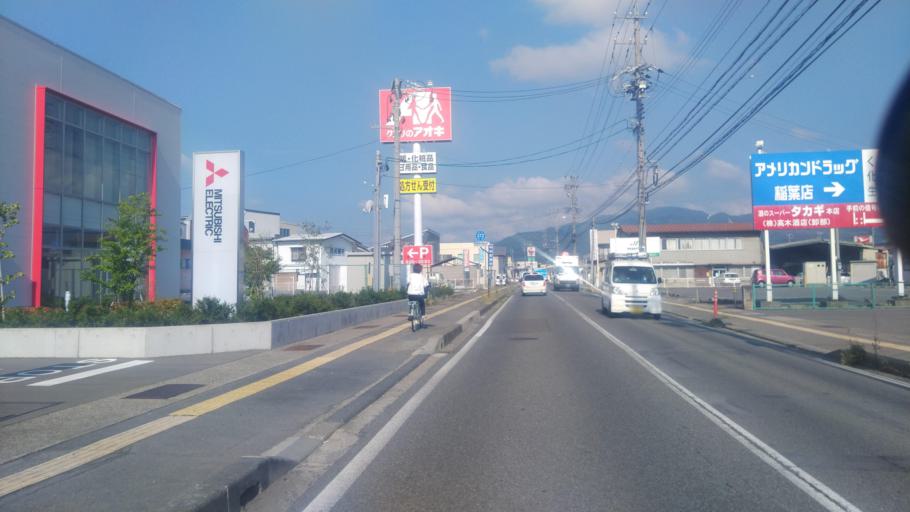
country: JP
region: Nagano
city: Nagano-shi
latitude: 36.6291
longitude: 138.2111
